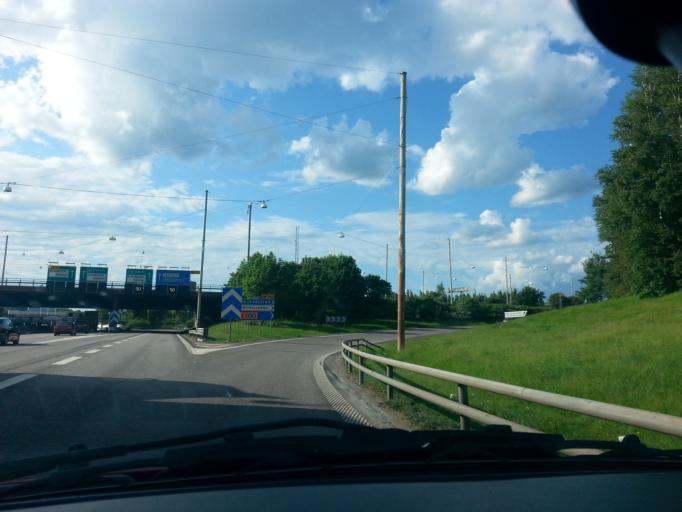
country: SE
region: Vaestra Goetaland
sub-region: Goteborg
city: Goeteborg
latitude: 57.7180
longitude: 11.9926
